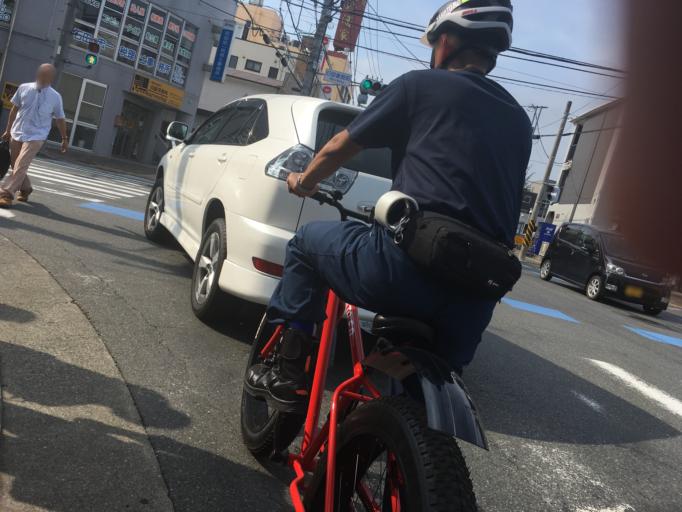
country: JP
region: Kanagawa
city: Minami-rinkan
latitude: 35.4748
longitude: 139.4622
